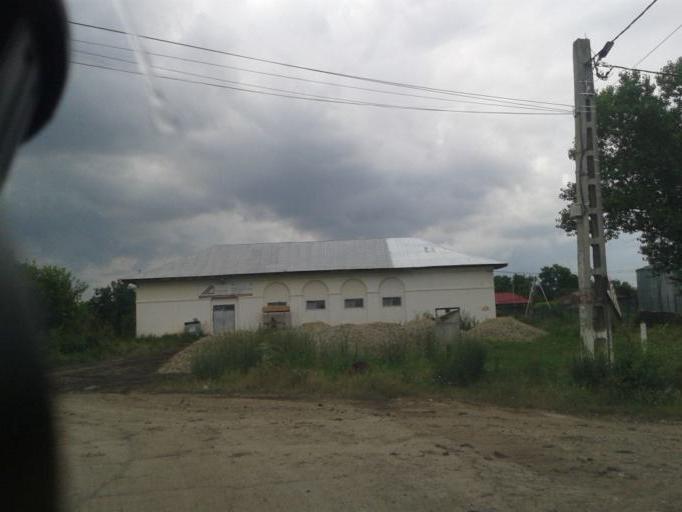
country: RO
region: Ialomita
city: Dragoesti-Snagov
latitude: 44.5330
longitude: 26.4833
